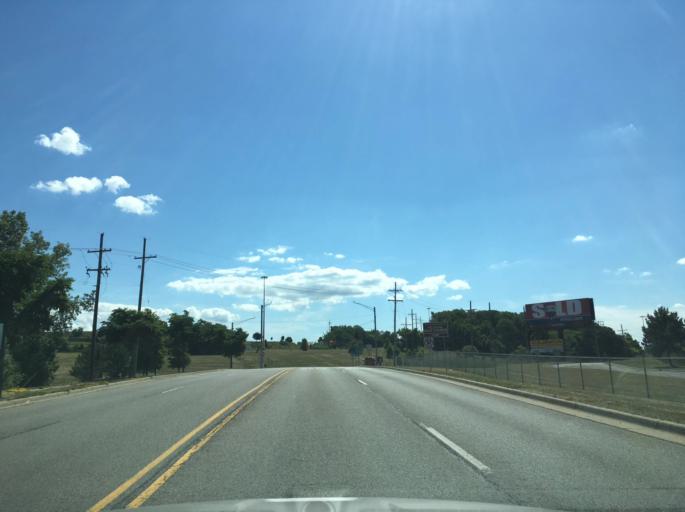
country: US
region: Michigan
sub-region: Oakland County
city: Auburn Hills
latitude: 42.6998
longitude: -83.2850
